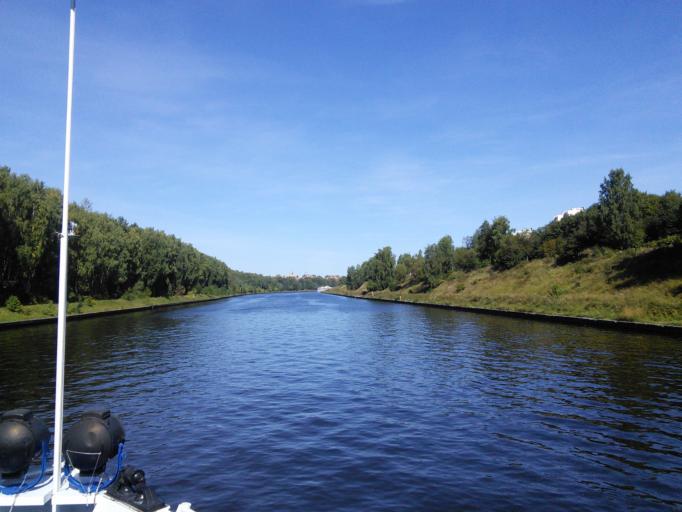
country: RU
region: Moskovskaya
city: Dolgoprudnyy
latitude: 55.9354
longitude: 37.4862
